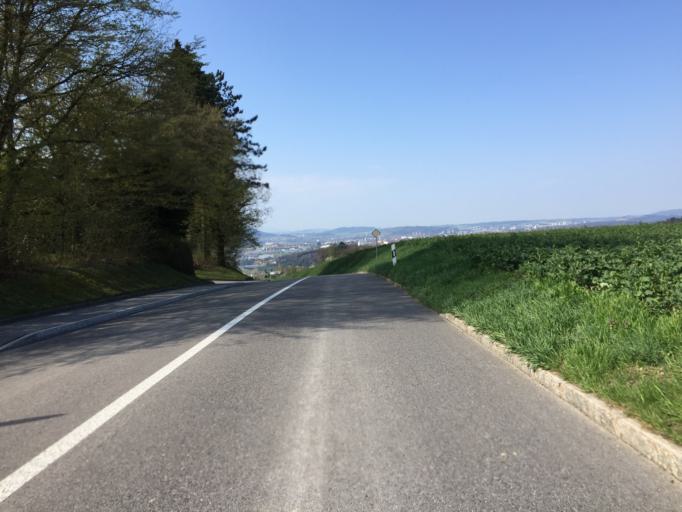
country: CH
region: Bern
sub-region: Bern-Mittelland District
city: Bolligen
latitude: 46.9860
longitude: 7.5074
